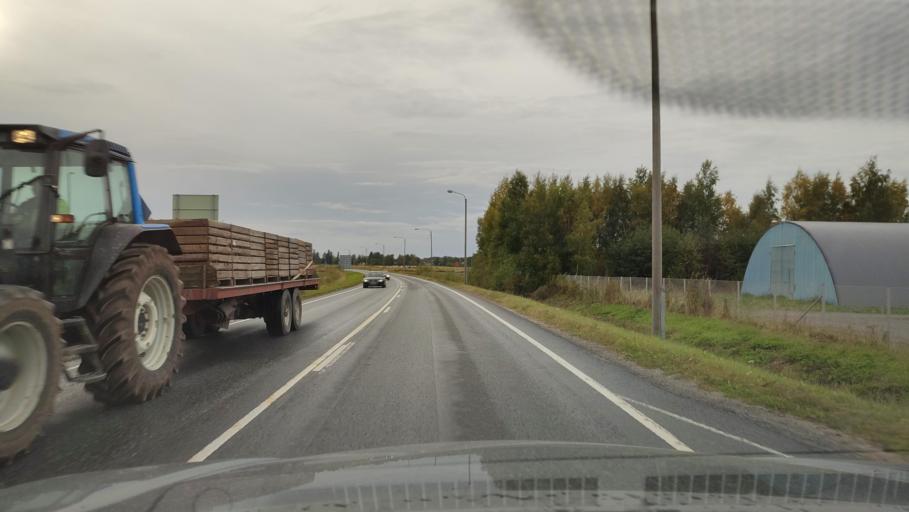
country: FI
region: Ostrobothnia
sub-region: Sydosterbotten
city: Kristinestad
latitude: 62.2617
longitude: 21.5275
